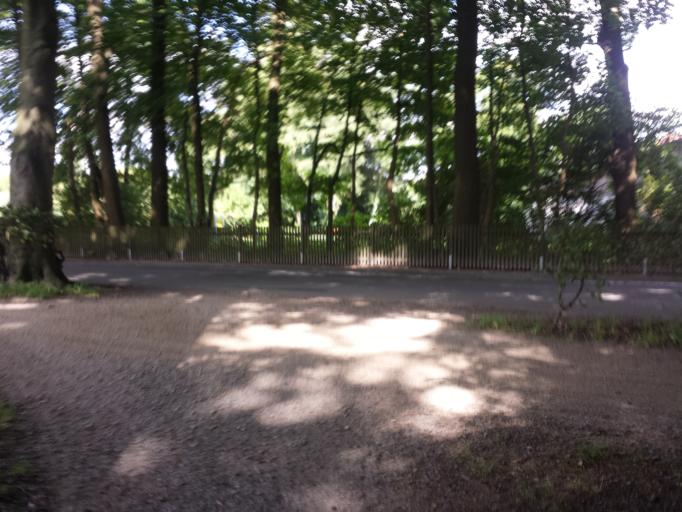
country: DE
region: North Rhine-Westphalia
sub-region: Regierungsbezirk Detmold
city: Guetersloh
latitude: 51.8964
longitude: 8.3953
